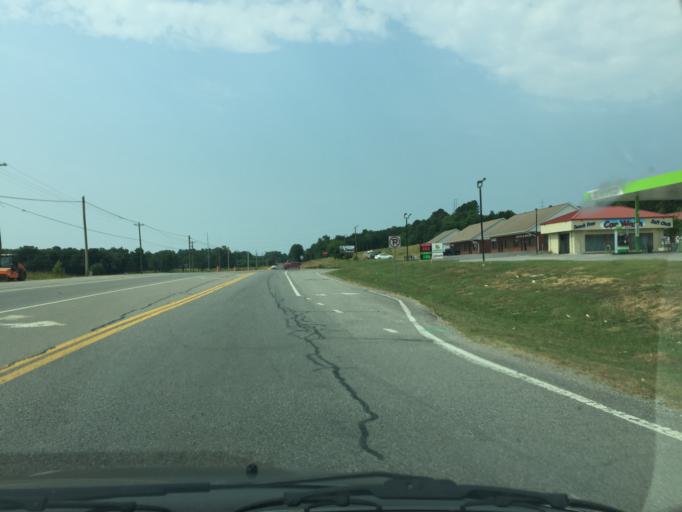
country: US
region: Georgia
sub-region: Catoosa County
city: Ringgold
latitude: 34.8959
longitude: -85.1312
